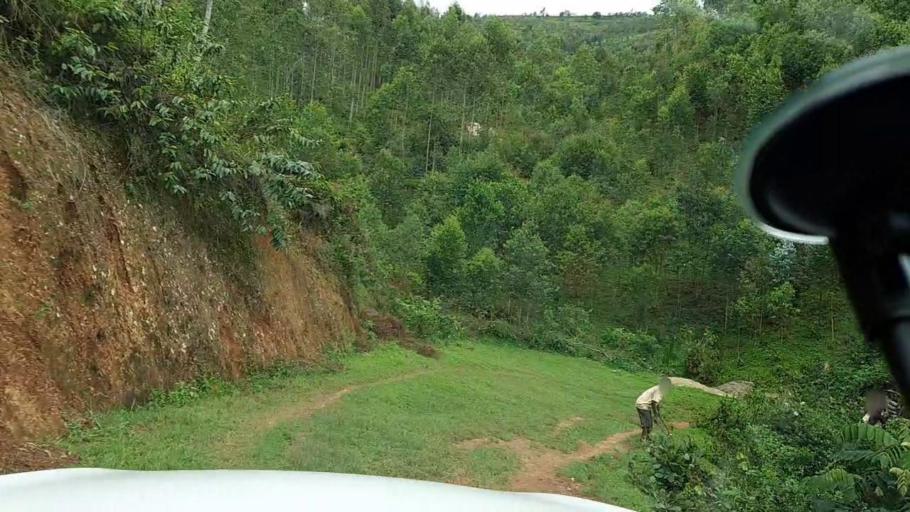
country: RW
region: Southern Province
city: Gitarama
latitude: -2.0756
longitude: 29.6444
